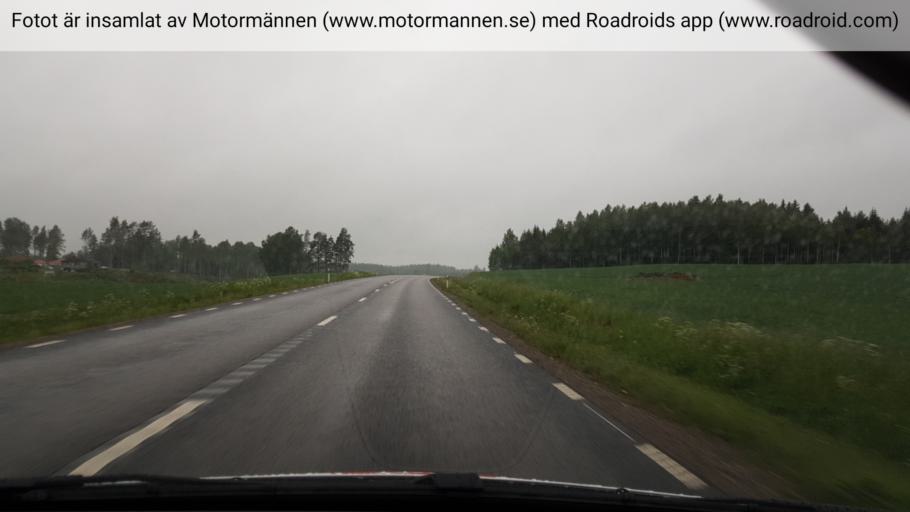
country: SE
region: OErebro
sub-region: Lindesbergs Kommun
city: Lindesberg
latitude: 59.5293
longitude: 15.2757
